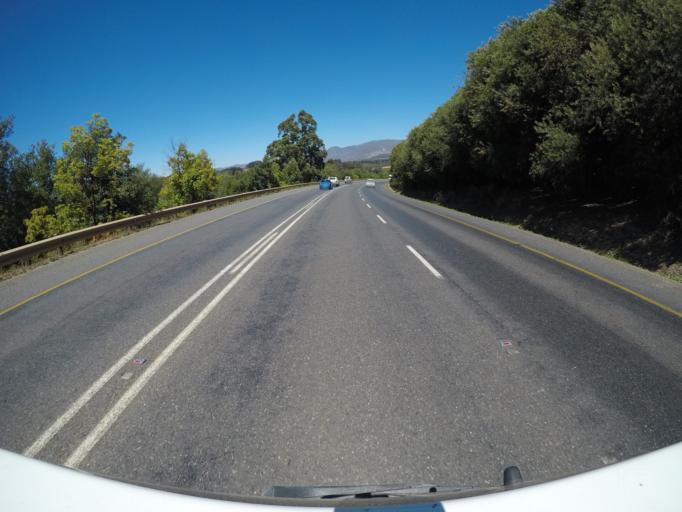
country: ZA
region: Western Cape
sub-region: Overberg District Municipality
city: Grabouw
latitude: -34.1641
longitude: 19.0269
